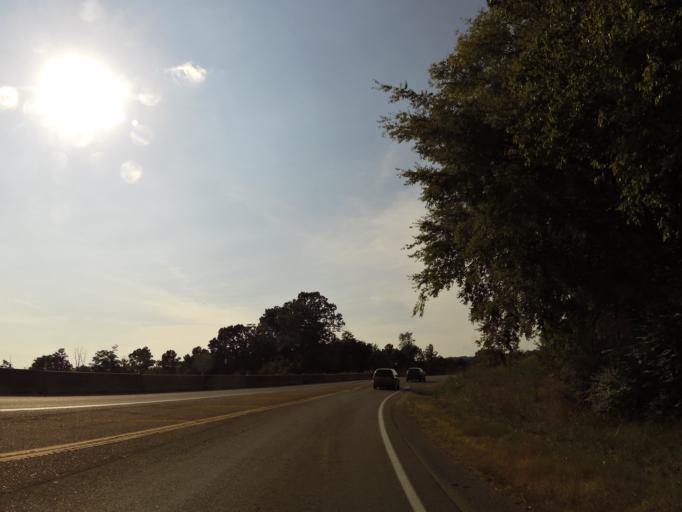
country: US
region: Tennessee
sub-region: Loudon County
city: Lenoir City
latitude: 35.7928
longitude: -84.2523
